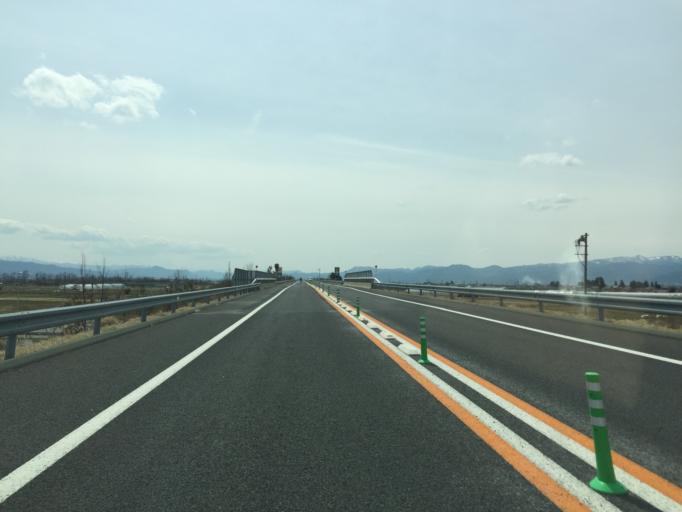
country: JP
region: Yamagata
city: Tendo
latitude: 38.3335
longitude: 140.3303
